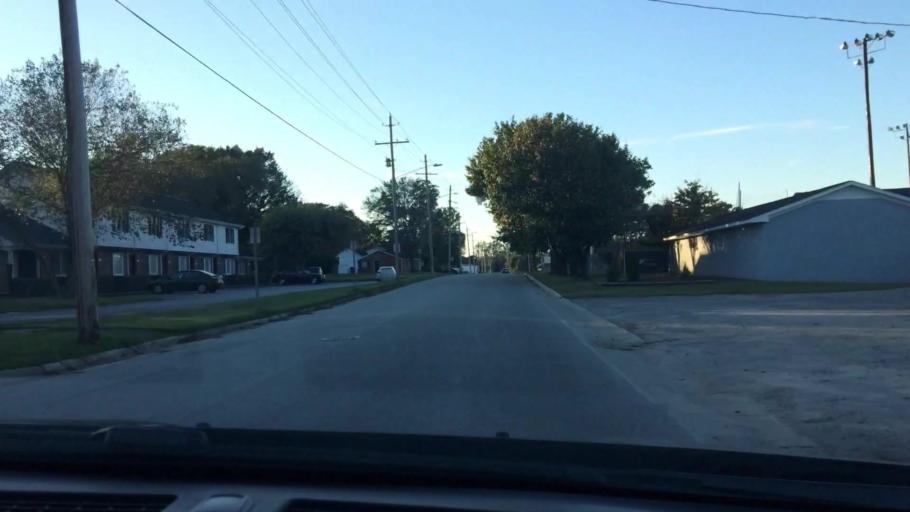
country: US
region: North Carolina
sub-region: Pitt County
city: Farmville
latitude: 35.6001
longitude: -77.5851
